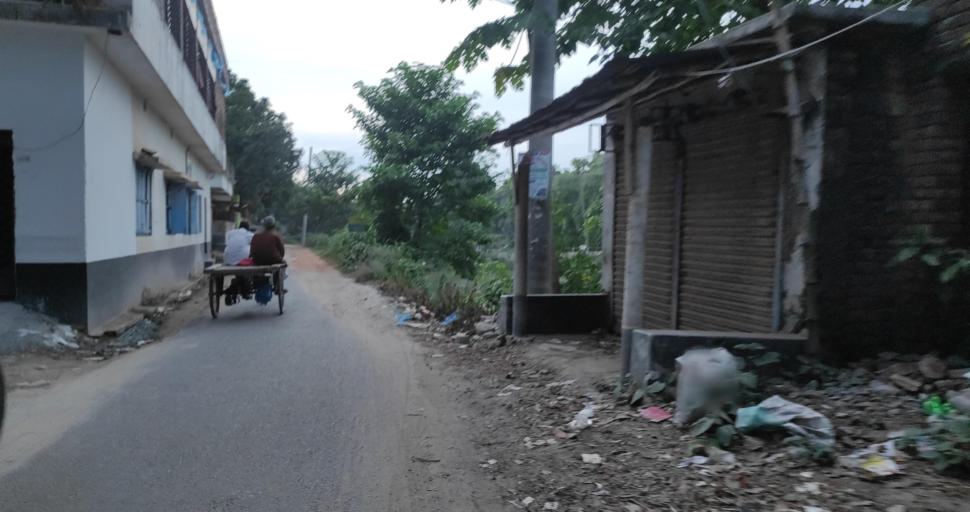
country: BD
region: Rajshahi
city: Par Naogaon
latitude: 24.5575
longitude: 88.9604
